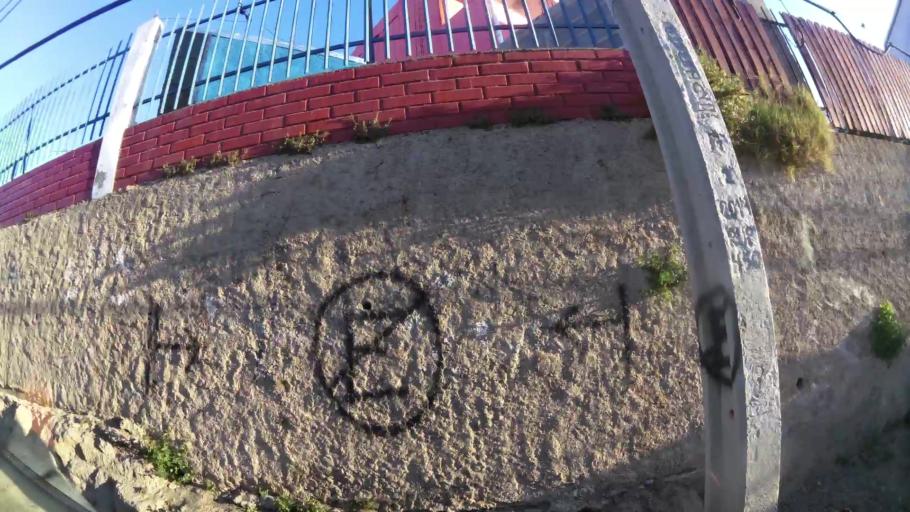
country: CL
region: Valparaiso
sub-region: Provincia de Valparaiso
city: Valparaiso
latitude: -33.0588
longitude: -71.6044
